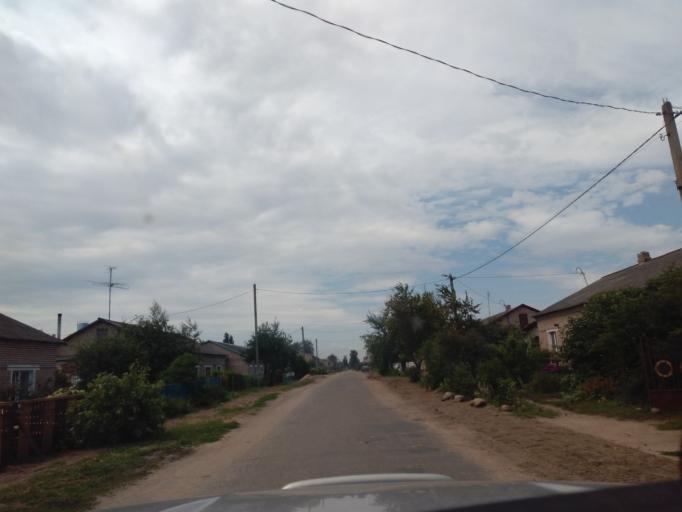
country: BY
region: Minsk
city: Kapyl'
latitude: 53.1416
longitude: 27.0946
